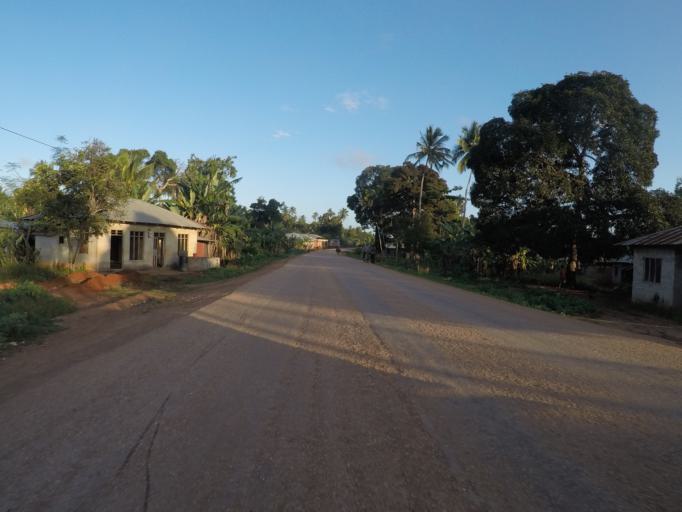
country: TZ
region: Zanzibar North
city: Gamba
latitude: -5.8989
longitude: 39.2943
